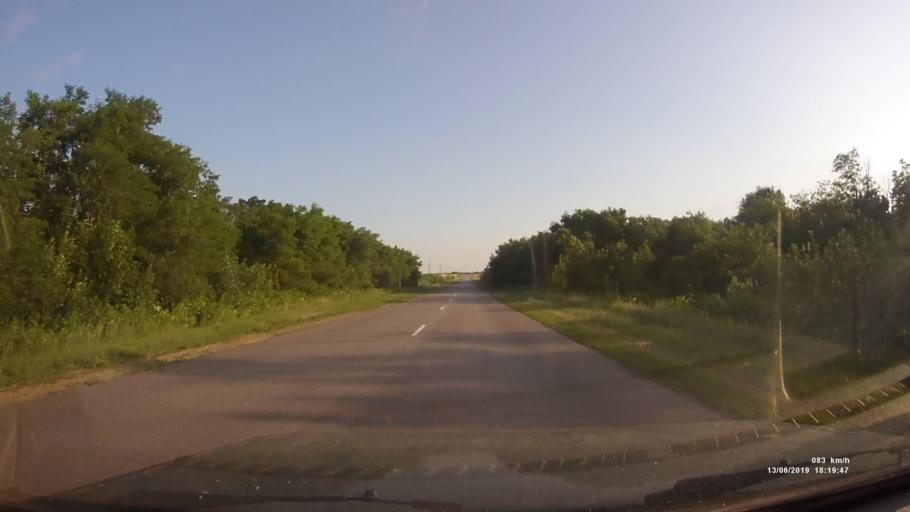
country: RU
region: Rostov
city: Kazanskaya
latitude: 49.8919
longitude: 41.3040
